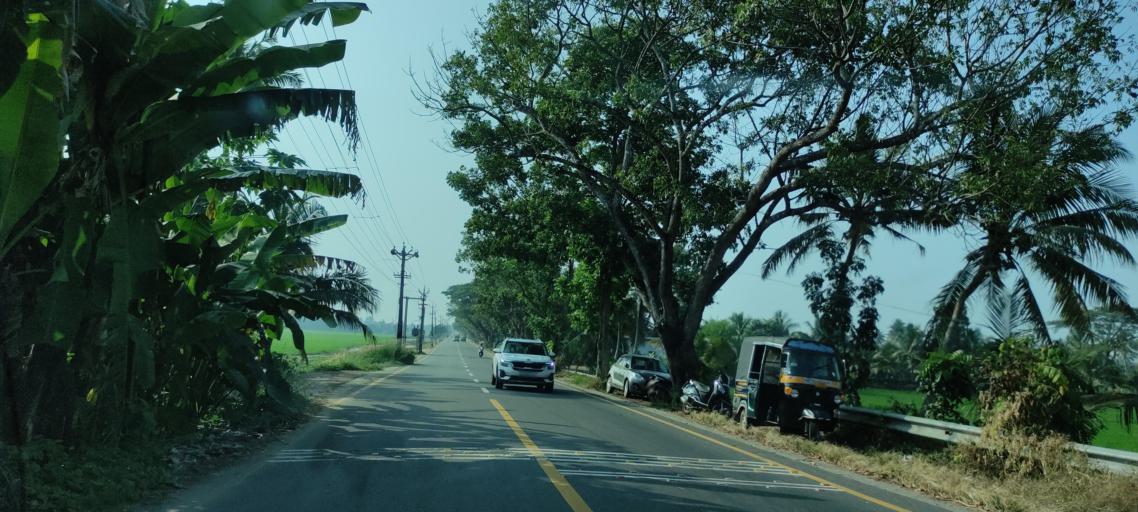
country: IN
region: Kerala
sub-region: Kottayam
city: Changanacheri
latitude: 9.3647
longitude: 76.4417
